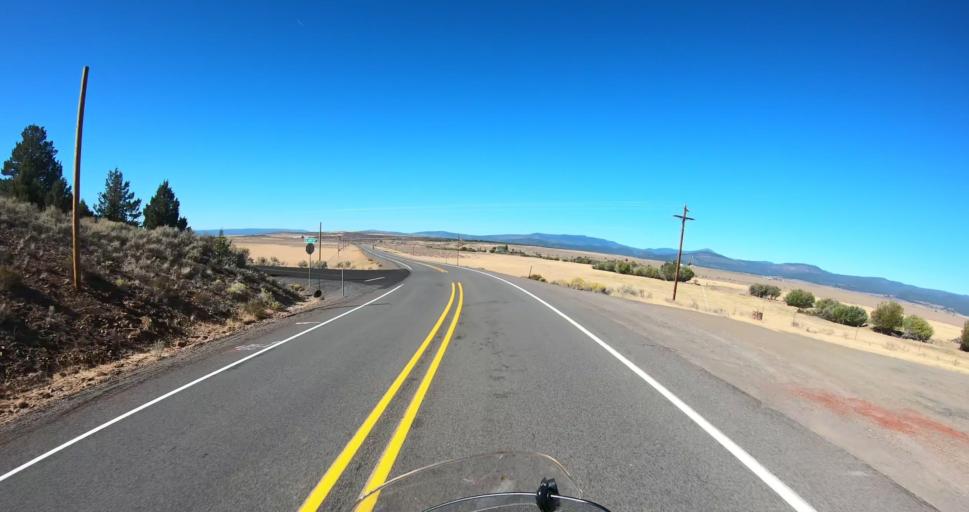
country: US
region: Oregon
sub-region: Lake County
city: Lakeview
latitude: 42.2618
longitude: -120.3465
